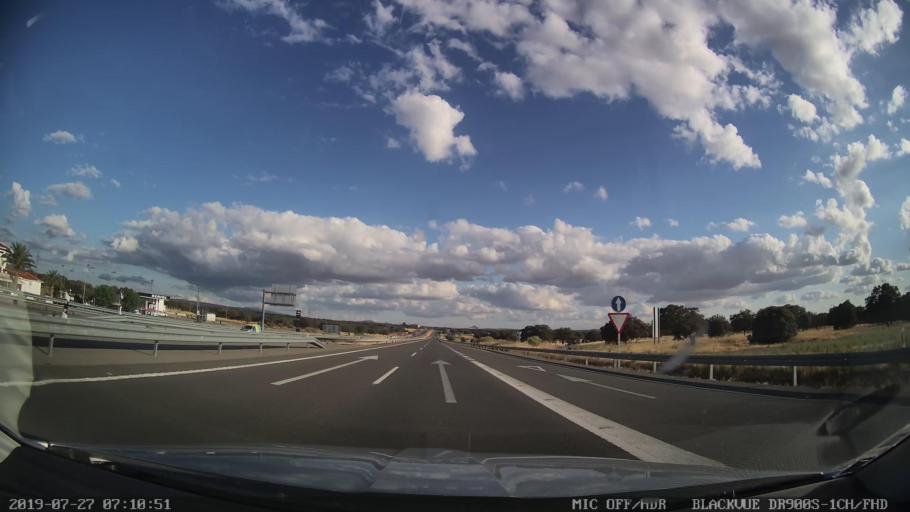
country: ES
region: Extremadura
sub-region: Provincia de Caceres
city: Torrecillas de la Tiesa
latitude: 39.5657
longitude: -5.8339
